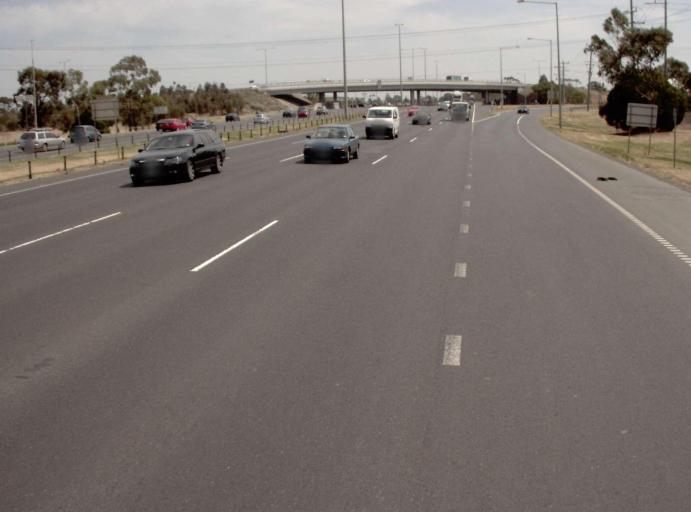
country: AU
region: Victoria
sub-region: Hobsons Bay
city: Laverton
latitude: -37.8428
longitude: 144.7886
